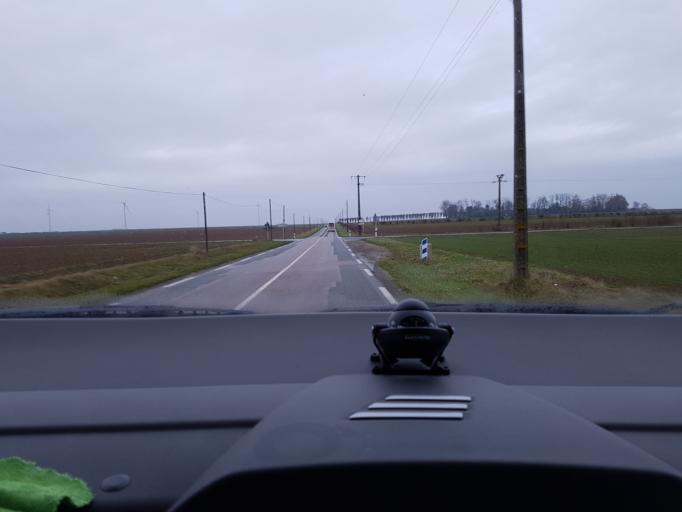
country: FR
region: Haute-Normandie
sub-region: Departement de l'Eure
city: Beaumont-le-Roger
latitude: 49.0926
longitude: 0.8029
